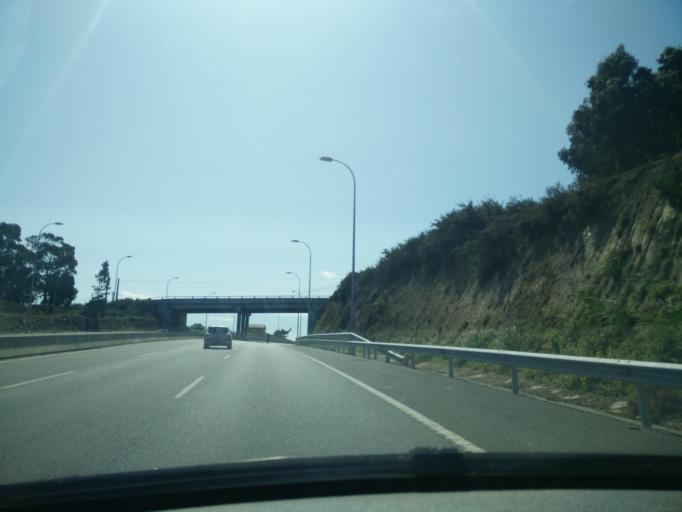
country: ES
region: Galicia
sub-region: Provincia da Coruna
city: A Coruna
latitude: 43.3619
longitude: -8.4328
